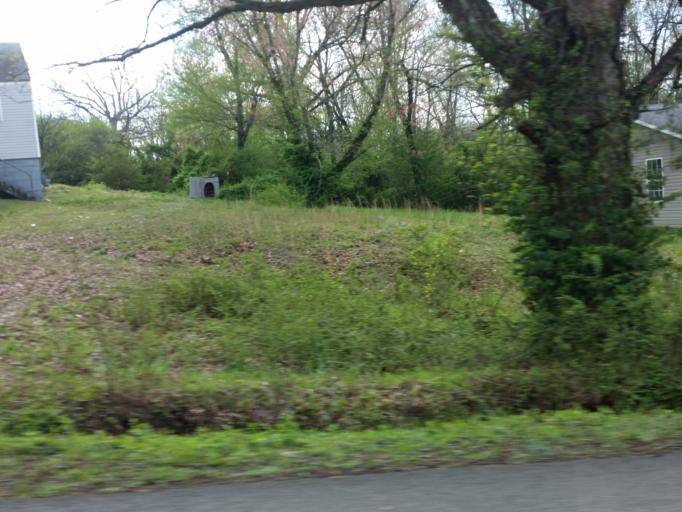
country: US
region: Missouri
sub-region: Butler County
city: Poplar Bluff
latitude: 36.7680
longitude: -90.3901
